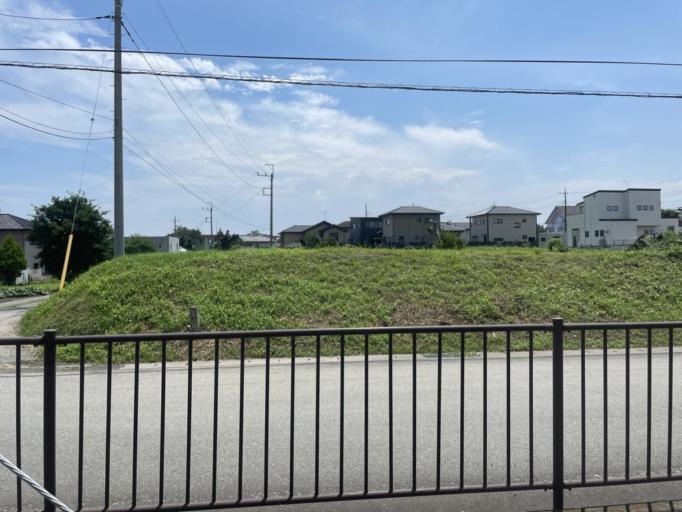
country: JP
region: Gunma
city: Omamacho-omama
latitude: 36.4186
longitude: 139.2364
